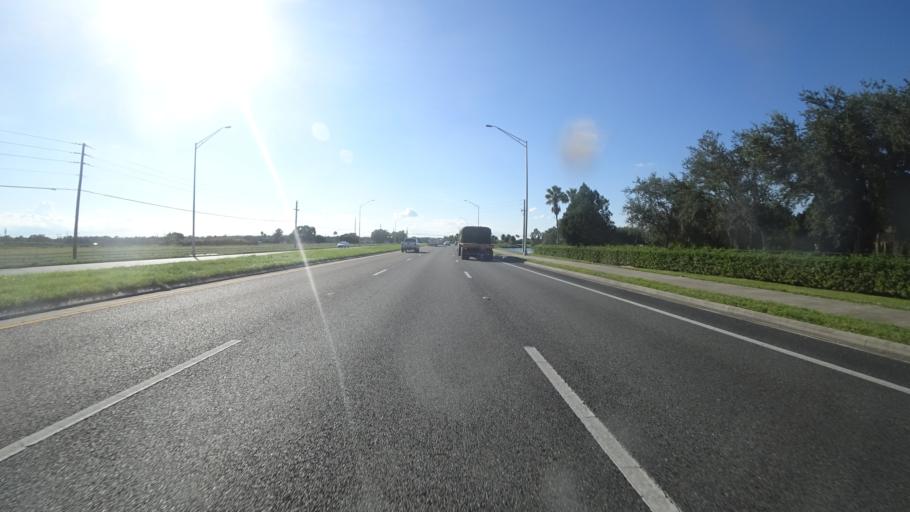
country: US
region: Florida
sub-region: Manatee County
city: Ellenton
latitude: 27.4861
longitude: -82.4487
